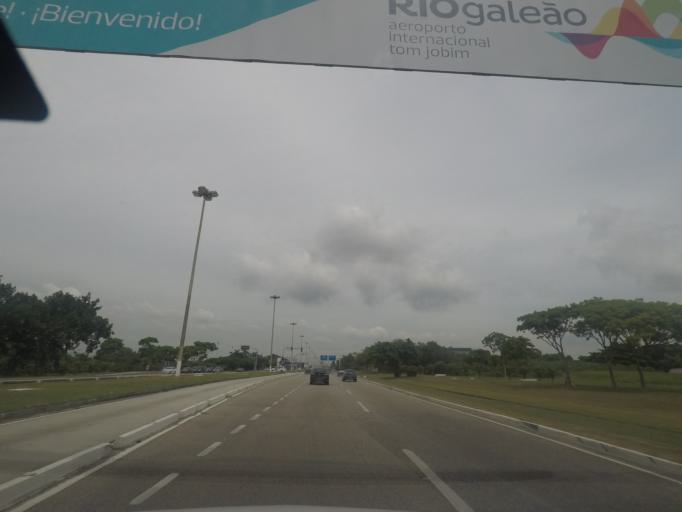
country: BR
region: Rio de Janeiro
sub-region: Duque De Caxias
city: Duque de Caxias
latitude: -22.8202
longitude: -43.2346
